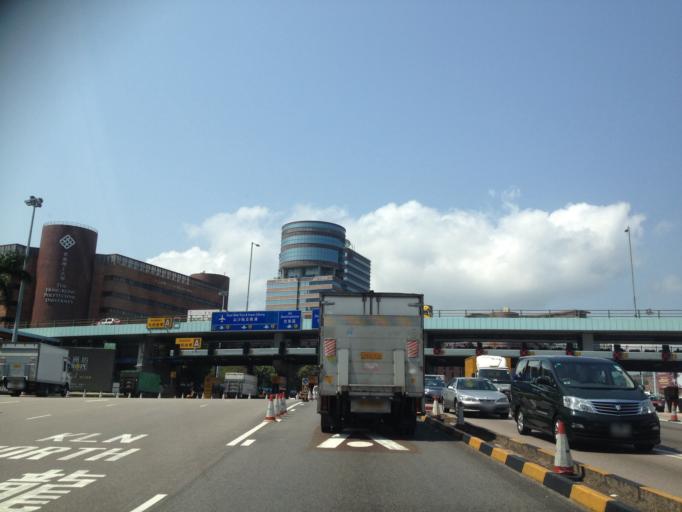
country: HK
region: Kowloon City
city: Kowloon
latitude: 22.3013
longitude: 114.1802
